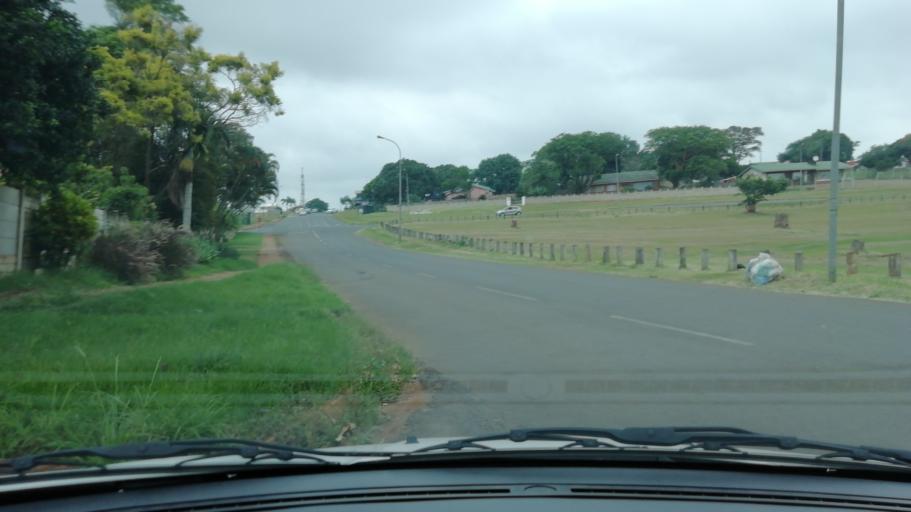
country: ZA
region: KwaZulu-Natal
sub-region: uThungulu District Municipality
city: Empangeni
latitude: -28.7377
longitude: 31.8972
